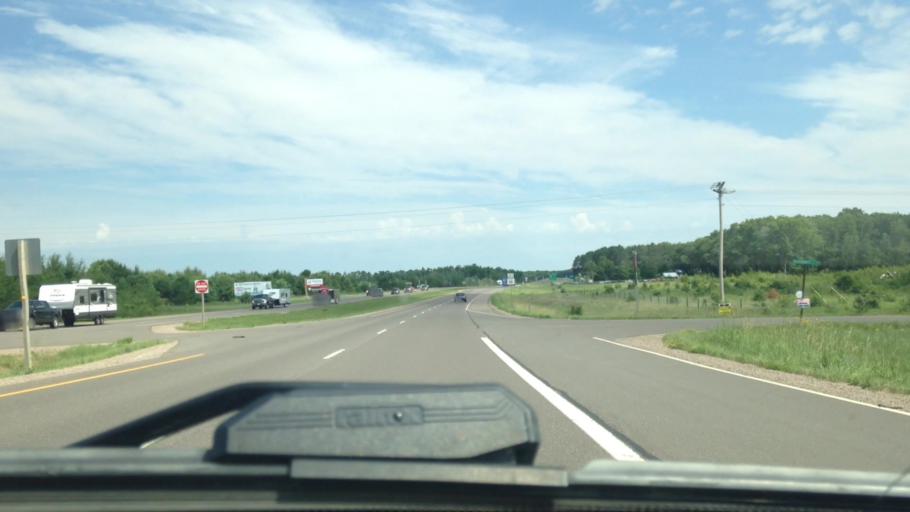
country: US
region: Wisconsin
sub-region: Washburn County
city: Spooner
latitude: 45.8393
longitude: -91.8609
